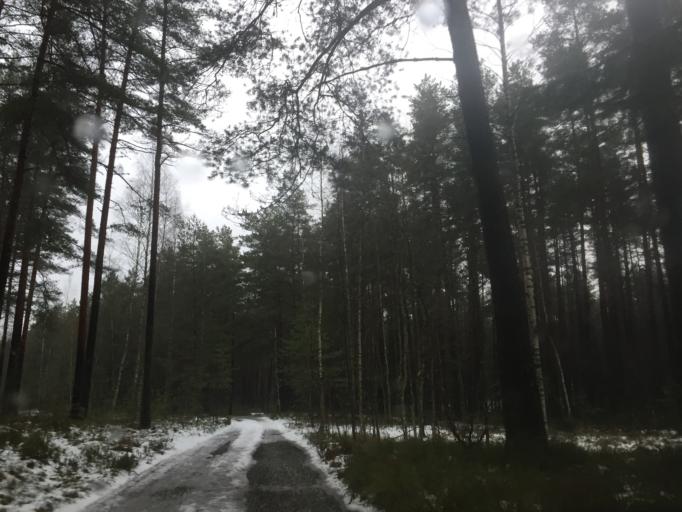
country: LV
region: Stopini
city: Ulbroka
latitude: 56.9516
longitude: 24.3358
